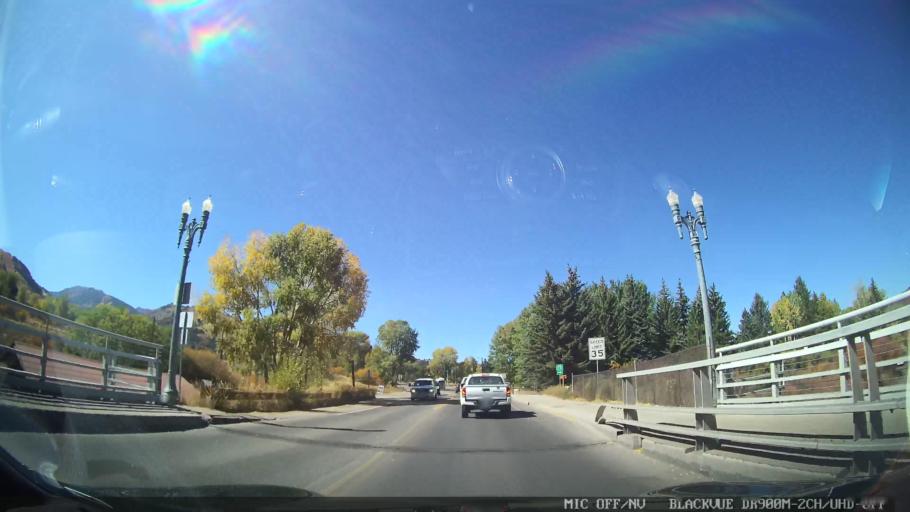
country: US
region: Colorado
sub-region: Pitkin County
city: Aspen
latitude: 39.1954
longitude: -106.8338
